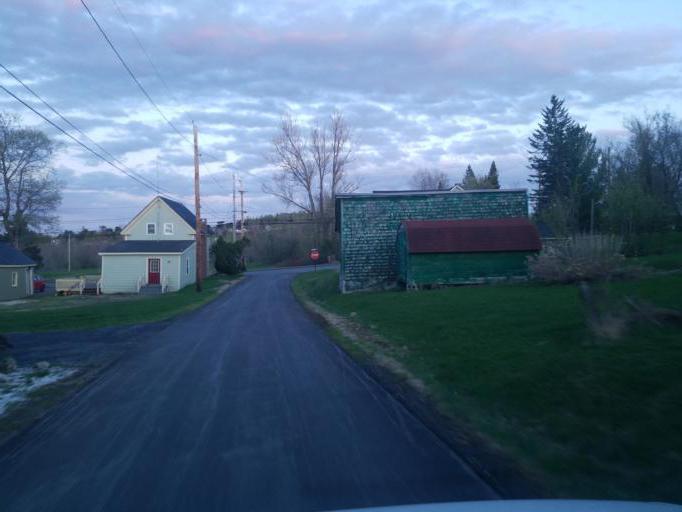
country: US
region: Maine
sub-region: Aroostook County
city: Caribou
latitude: 46.8578
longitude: -68.0229
